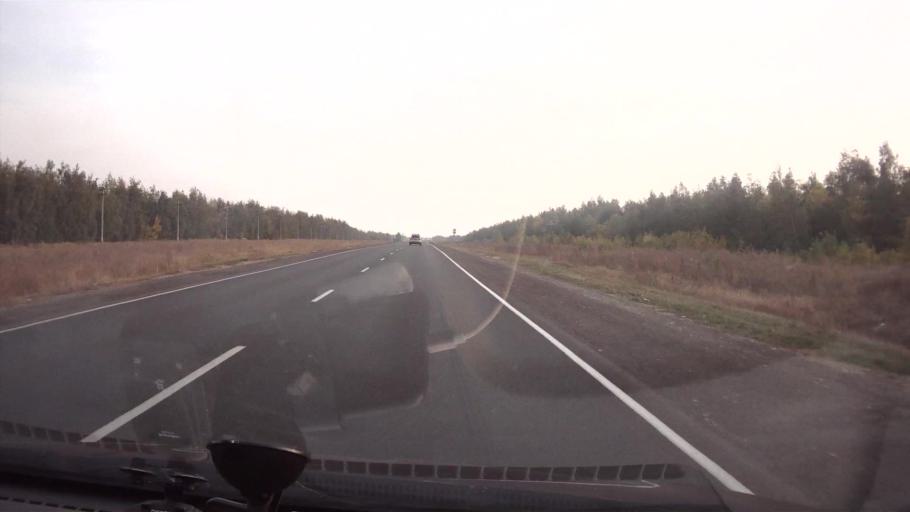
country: RU
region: Saratov
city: Krasnyy Oktyabr'
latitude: 51.3747
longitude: 45.7124
